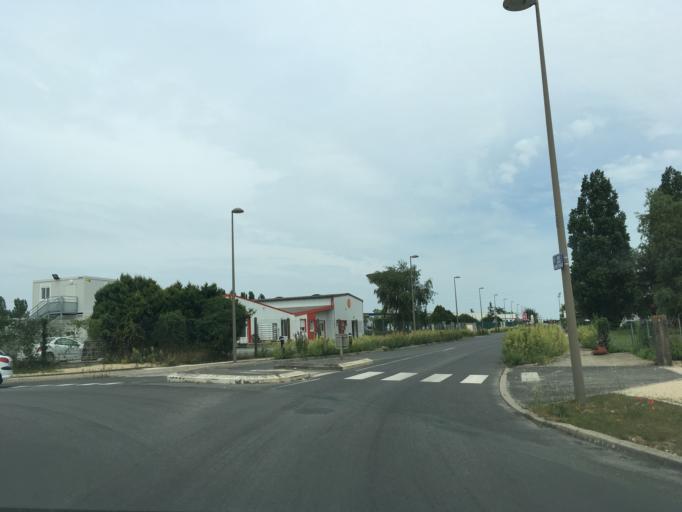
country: FR
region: Poitou-Charentes
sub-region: Departement des Deux-Sevres
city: Bessines
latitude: 46.3139
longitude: -0.4986
